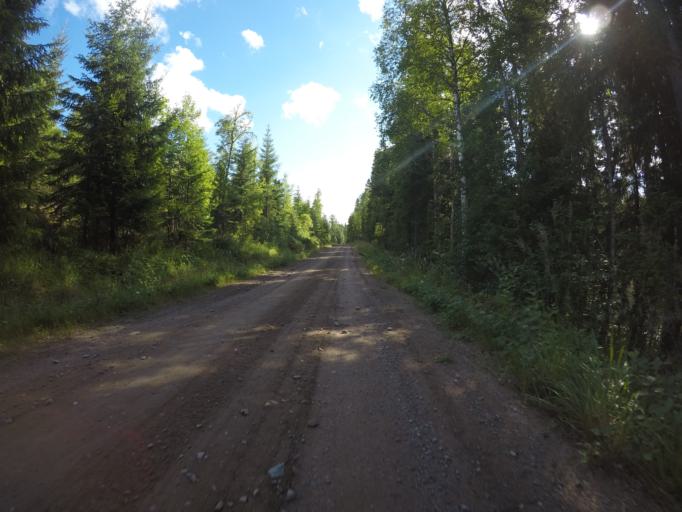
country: SE
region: OErebro
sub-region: Hallefors Kommun
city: Haellefors
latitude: 60.0040
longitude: 14.6084
